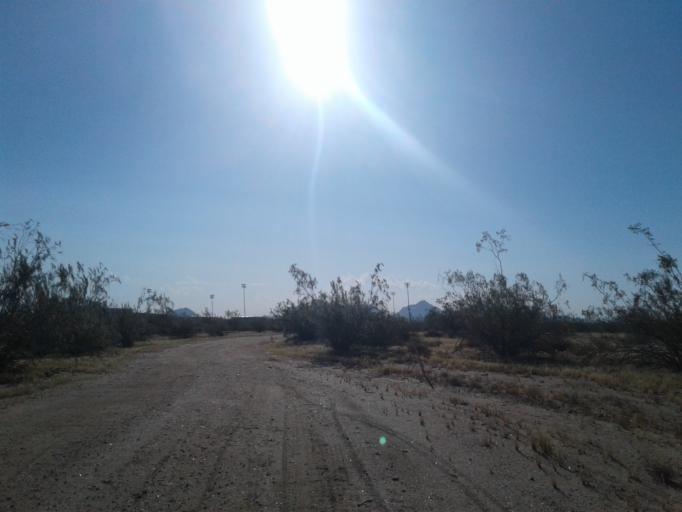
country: US
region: Arizona
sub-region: Maricopa County
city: Paradise Valley
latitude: 33.6789
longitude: -112.0136
